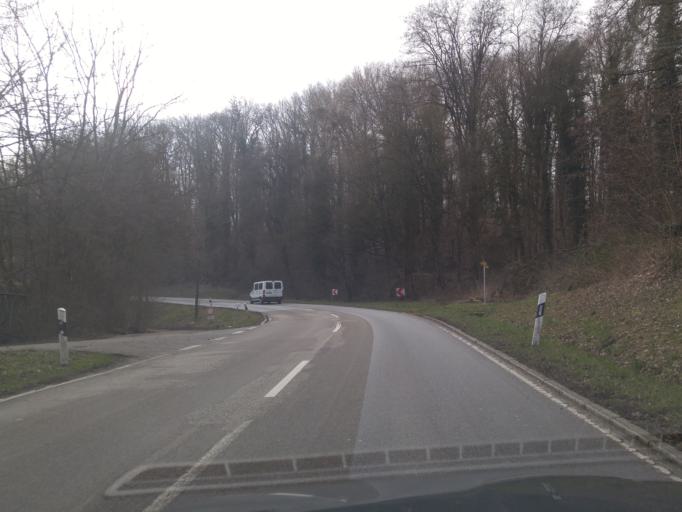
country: DE
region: Baden-Wuerttemberg
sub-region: Regierungsbezirk Stuttgart
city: Flein
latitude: 49.0874
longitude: 9.2218
